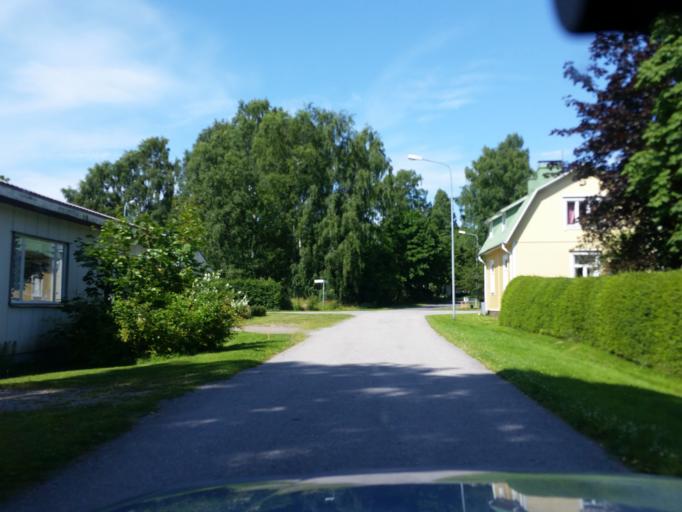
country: FI
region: Uusimaa
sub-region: Raaseporin
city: Hanko
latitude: 59.8355
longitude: 22.9462
